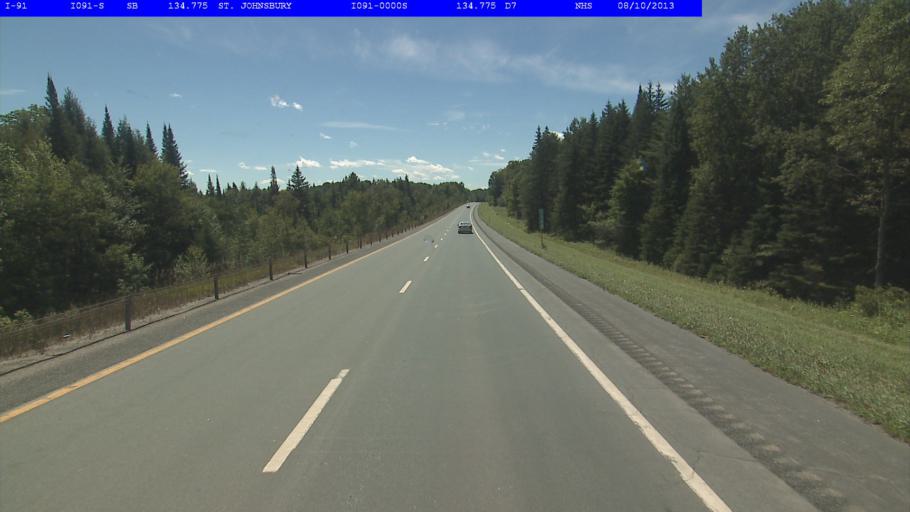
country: US
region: Vermont
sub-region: Caledonia County
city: Lyndon
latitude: 44.4861
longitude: -72.0223
